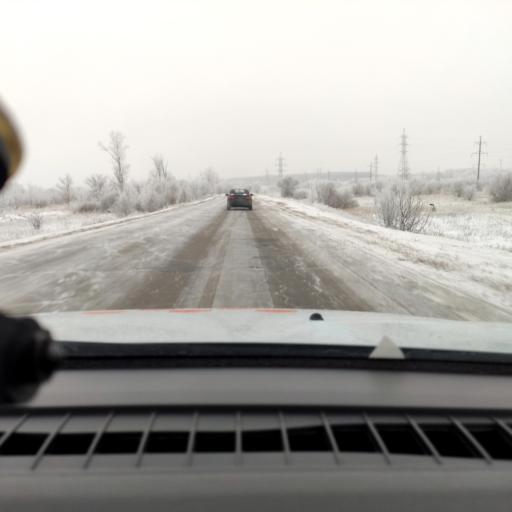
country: RU
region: Samara
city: Samara
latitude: 53.1078
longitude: 50.2261
